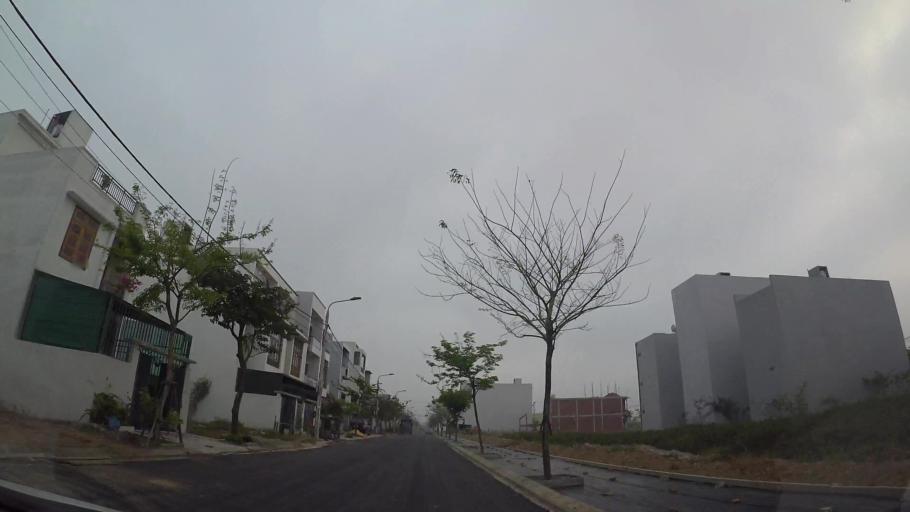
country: VN
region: Da Nang
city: Ngu Hanh Son
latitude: 16.0207
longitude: 108.2331
